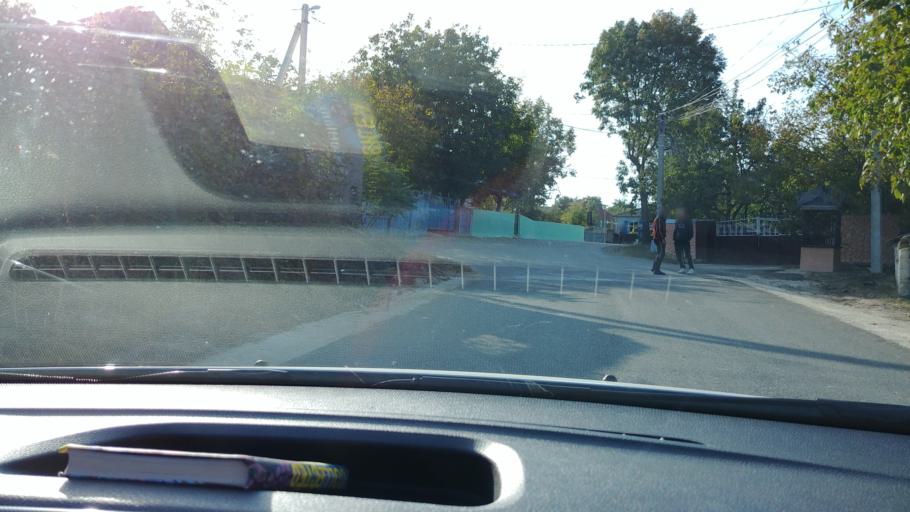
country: MD
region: Rezina
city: Rezina
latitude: 47.7492
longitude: 28.8831
